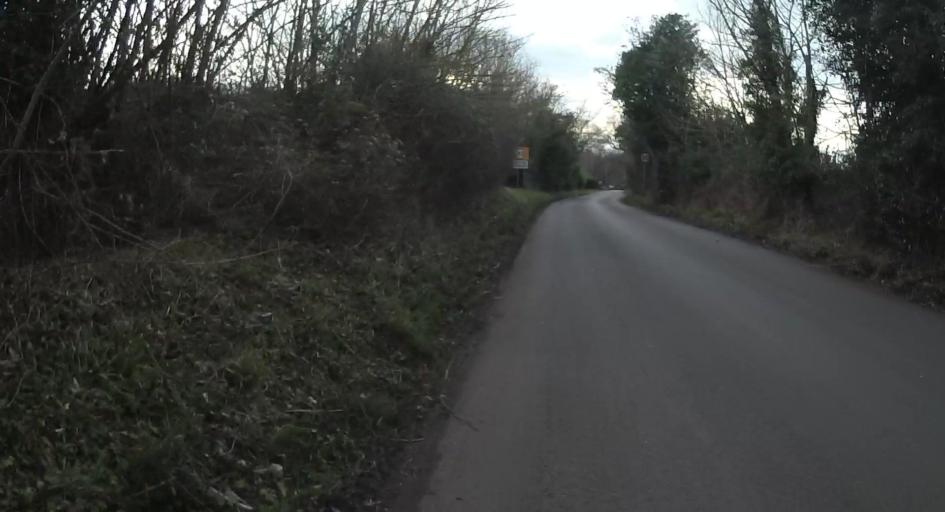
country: GB
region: England
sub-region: West Berkshire
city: Theale
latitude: 51.4012
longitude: -1.0819
